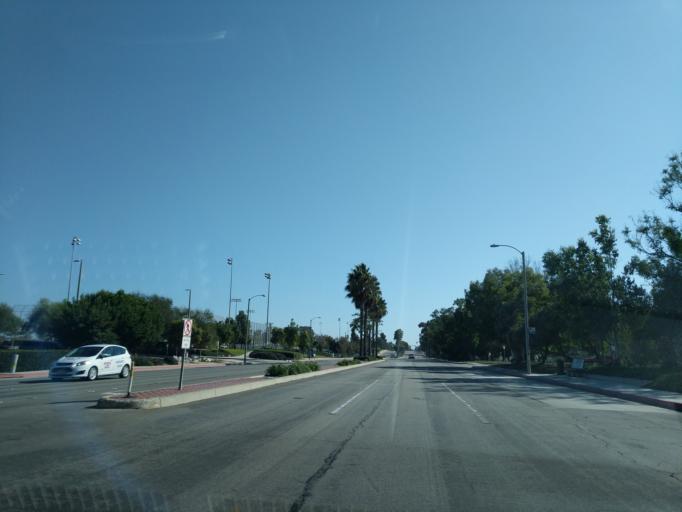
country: US
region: California
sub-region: Orange County
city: Huntington Beach
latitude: 33.6993
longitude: -118.0065
